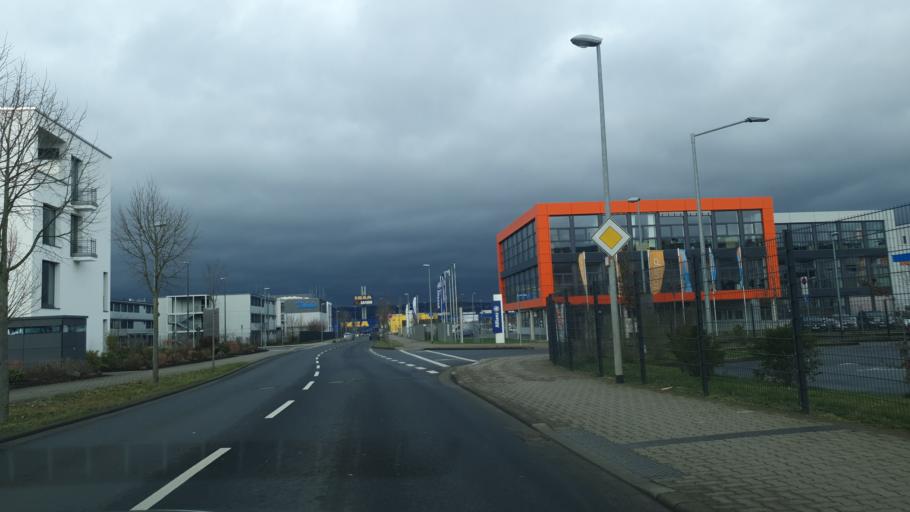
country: DE
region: Rheinland-Pfalz
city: Koblenz
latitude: 50.3779
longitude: 7.5641
